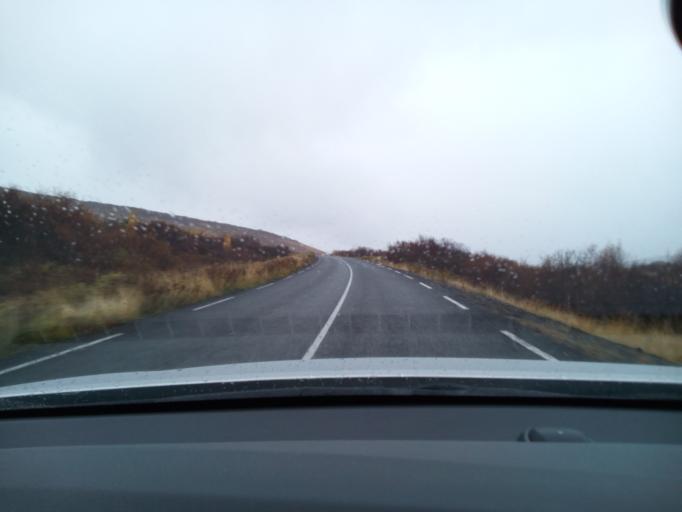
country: IS
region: South
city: Hveragerdi
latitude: 64.7024
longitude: -20.9959
